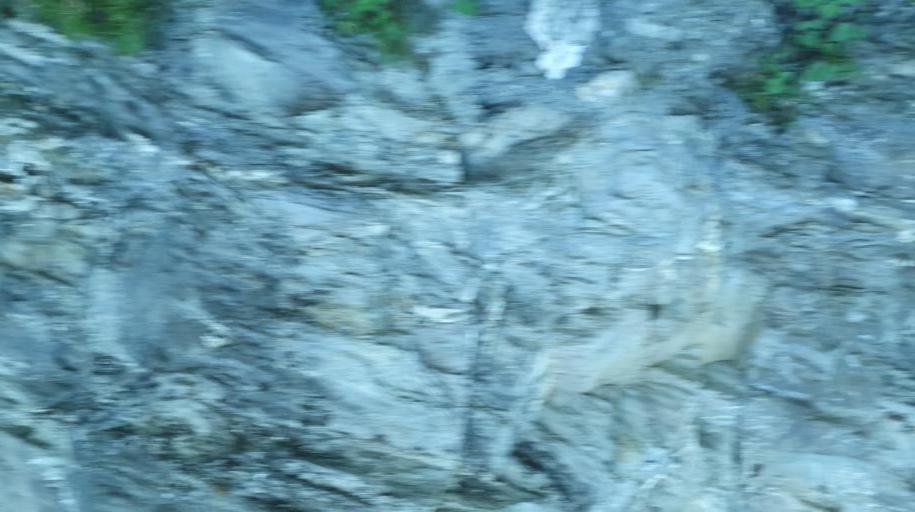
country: NO
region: Nord-Trondelag
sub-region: Verdal
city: Verdal
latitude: 63.7728
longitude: 11.4078
